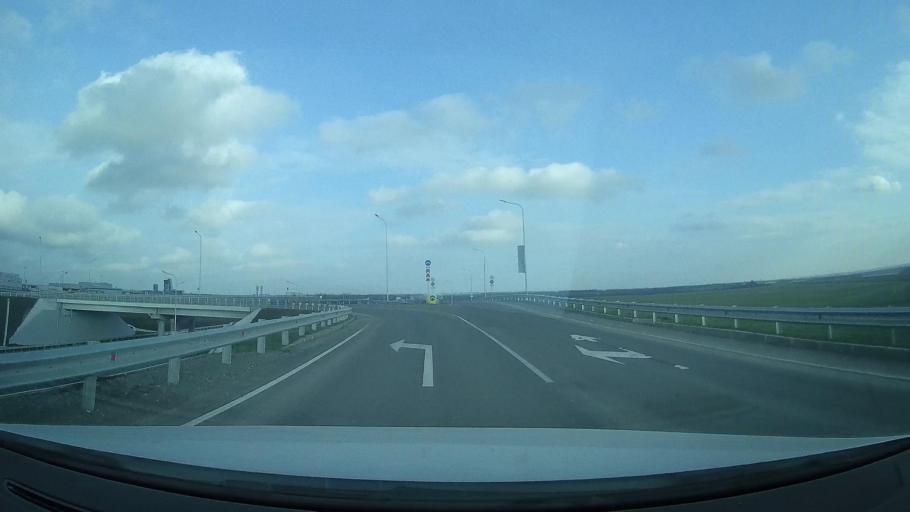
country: RU
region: Rostov
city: Grushevskaya
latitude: 47.4859
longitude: 39.9358
